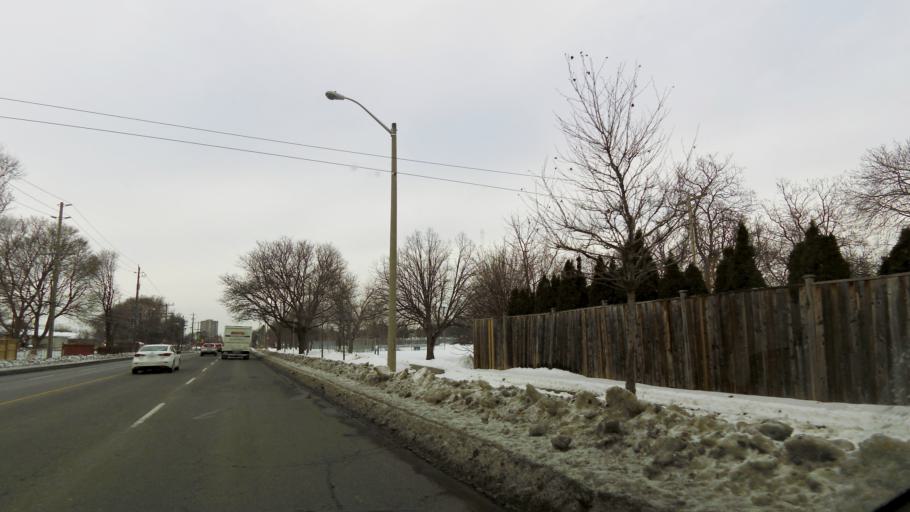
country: CA
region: Ontario
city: Etobicoke
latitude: 43.6865
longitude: -79.5419
